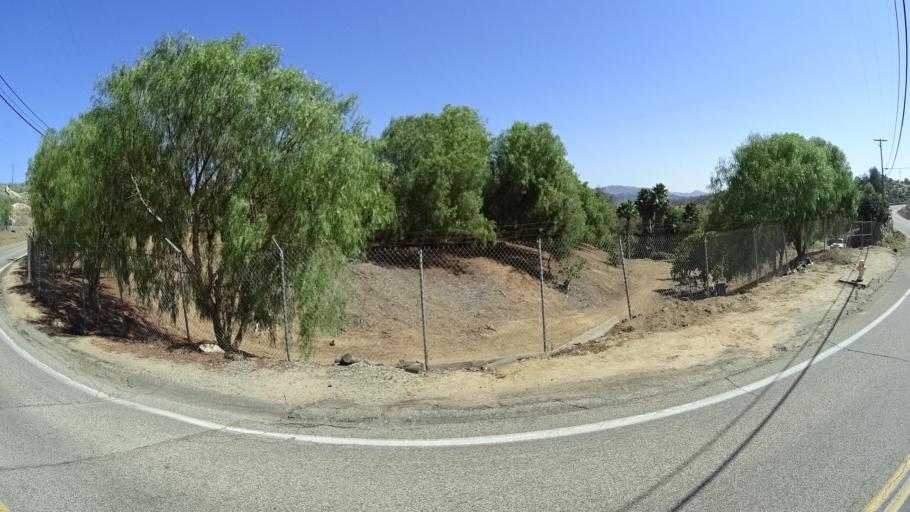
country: US
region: California
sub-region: San Diego County
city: Hidden Meadows
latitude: 33.3010
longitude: -117.1419
